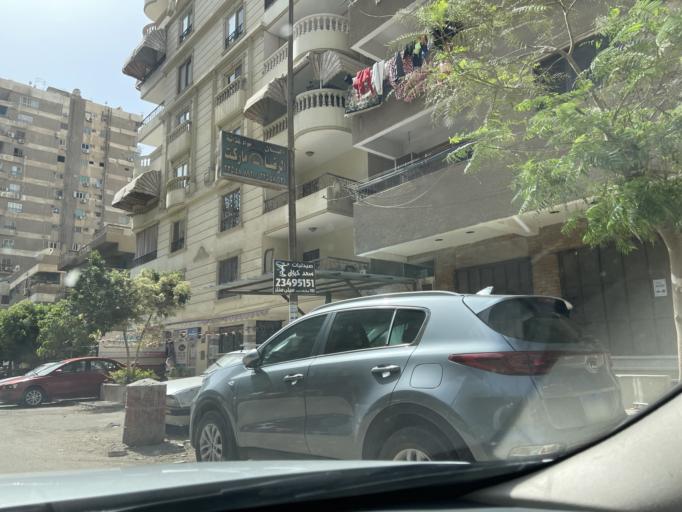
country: EG
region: Muhafazat al Qahirah
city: Cairo
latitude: 30.0646
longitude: 31.3523
